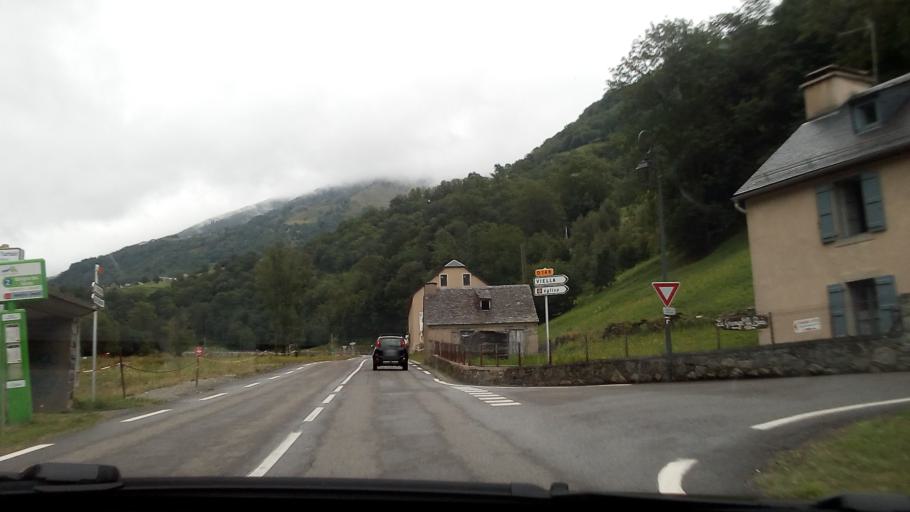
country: FR
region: Midi-Pyrenees
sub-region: Departement des Hautes-Pyrenees
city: Luz-Saint-Sauveur
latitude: 42.8784
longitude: 0.0195
